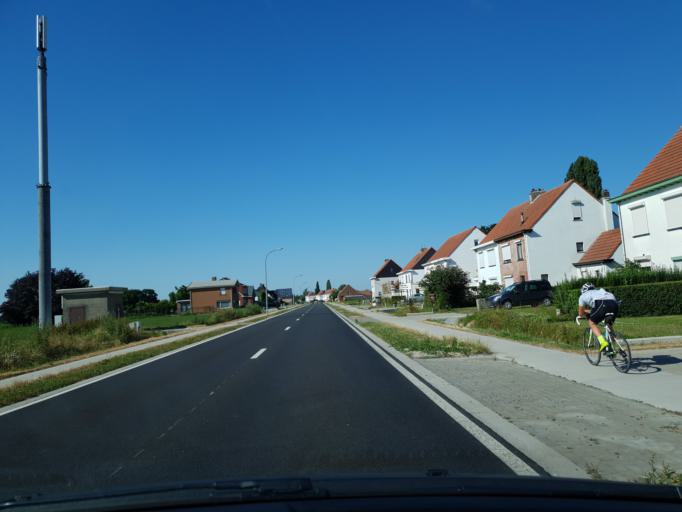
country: BE
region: Flanders
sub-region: Provincie Antwerpen
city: Merksplas
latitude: 51.3436
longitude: 4.8614
